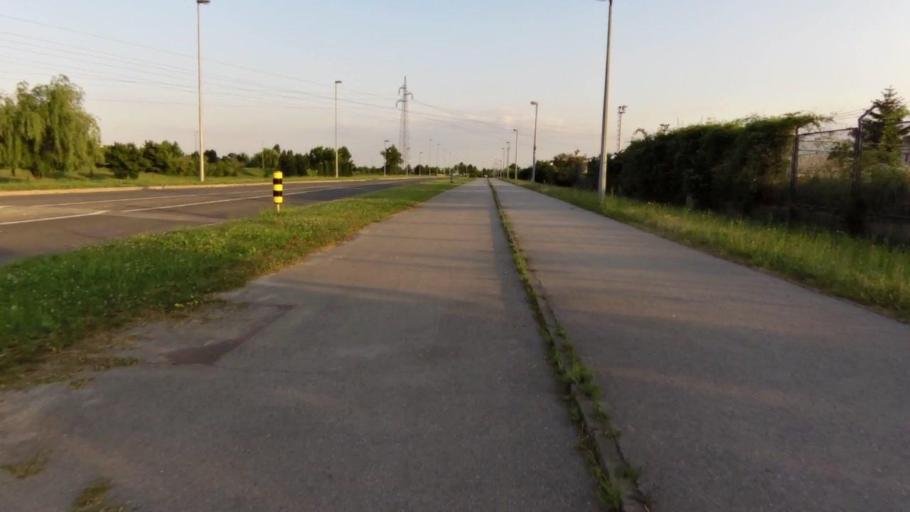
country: HR
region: Zagrebacka
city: Micevec
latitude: 45.7915
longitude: 16.0790
